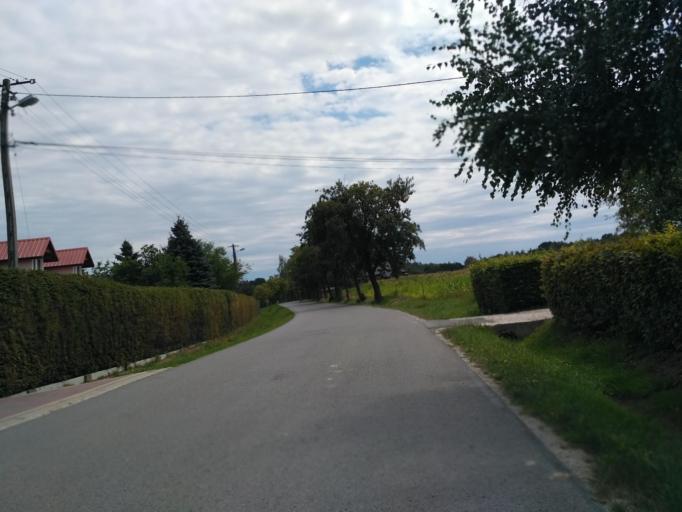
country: PL
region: Subcarpathian Voivodeship
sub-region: Powiat rzeszowski
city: Chmielnik
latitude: 49.9542
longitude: 22.1345
